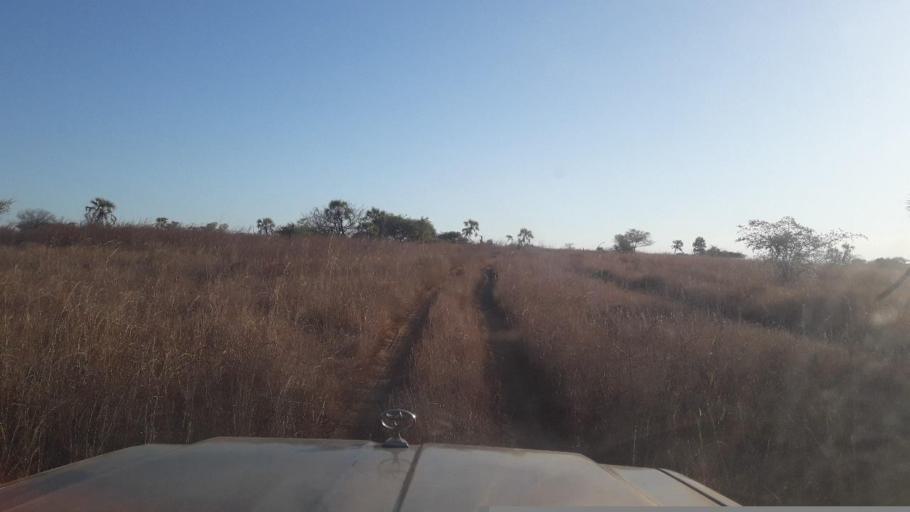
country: MG
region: Boeny
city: Sitampiky
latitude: -16.4984
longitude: 45.6056
